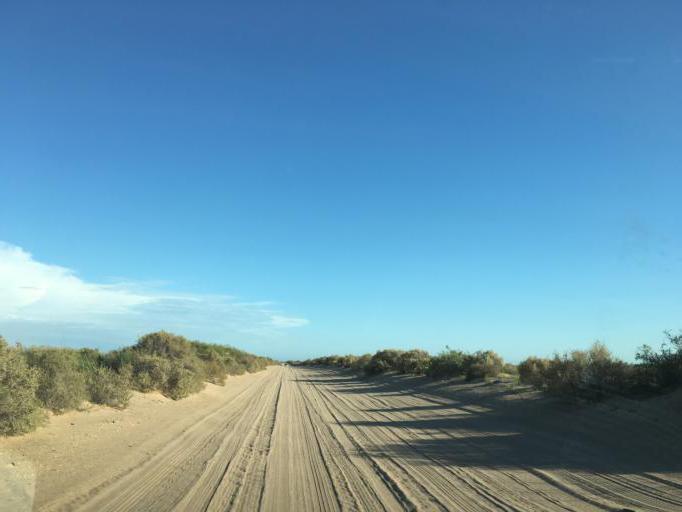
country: MX
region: Sonora
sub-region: Puerto Penasco
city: Puerto Penasco
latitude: 31.3149
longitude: -113.4506
